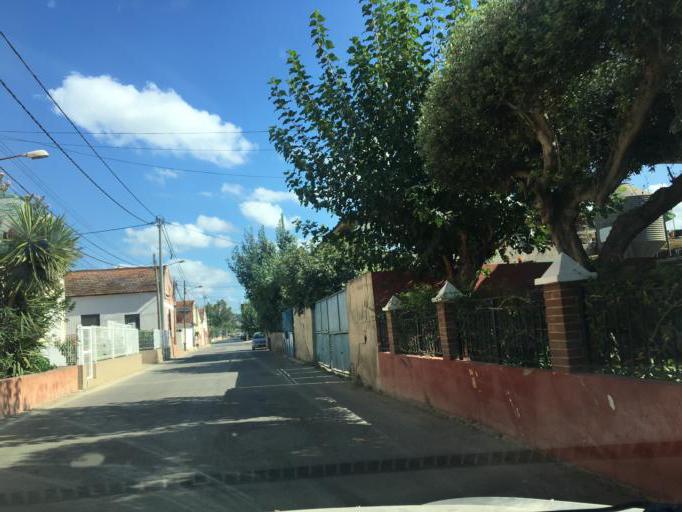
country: ES
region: Murcia
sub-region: Murcia
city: Santomera
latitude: 38.0276
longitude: -1.0475
